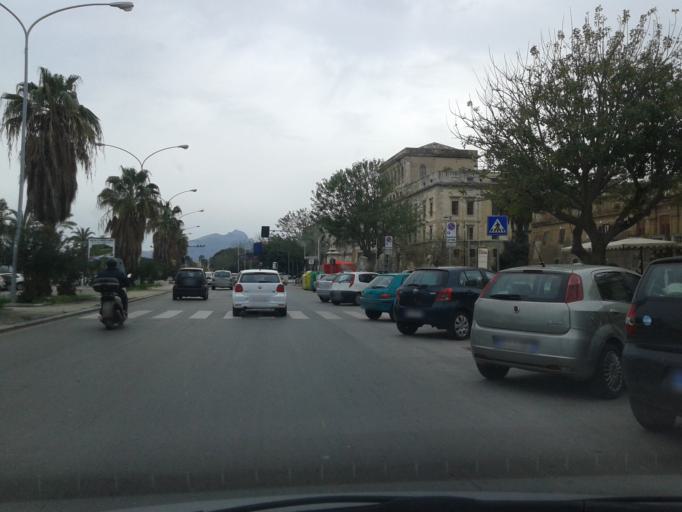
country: IT
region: Sicily
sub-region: Palermo
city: Palermo
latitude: 38.1173
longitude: 13.3733
